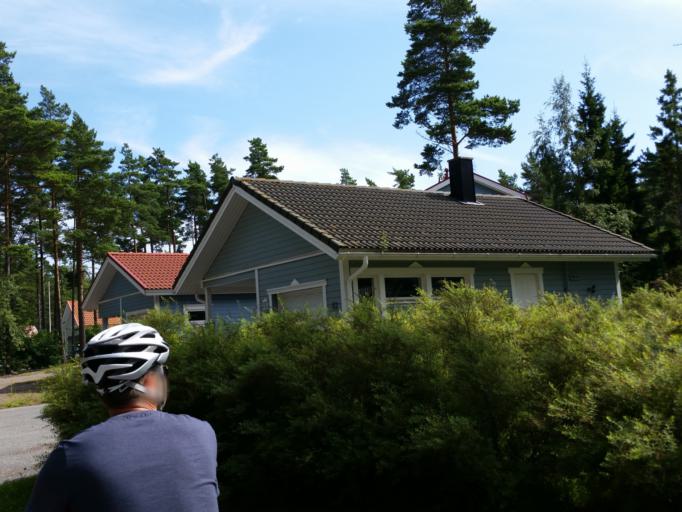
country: FI
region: Uusimaa
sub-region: Raaseporin
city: Hanko
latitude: 59.8442
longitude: 22.9361
